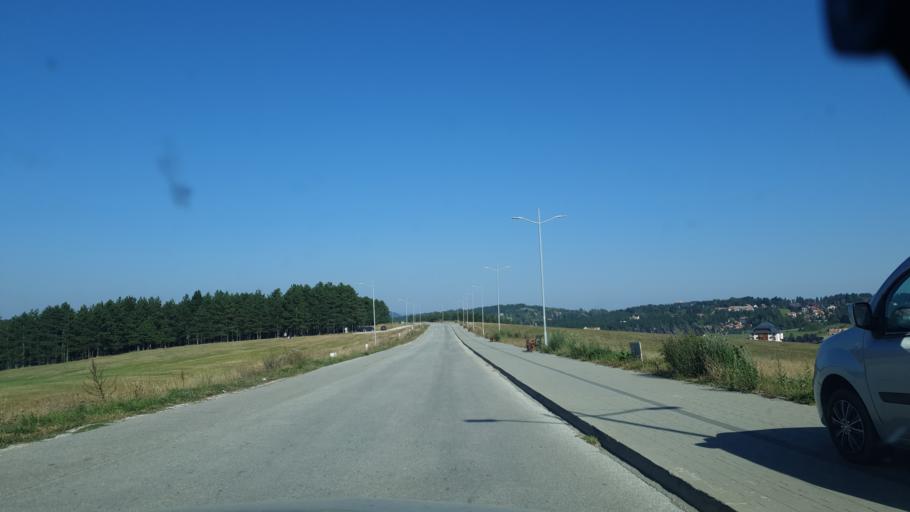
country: RS
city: Zlatibor
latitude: 43.7184
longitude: 19.7150
